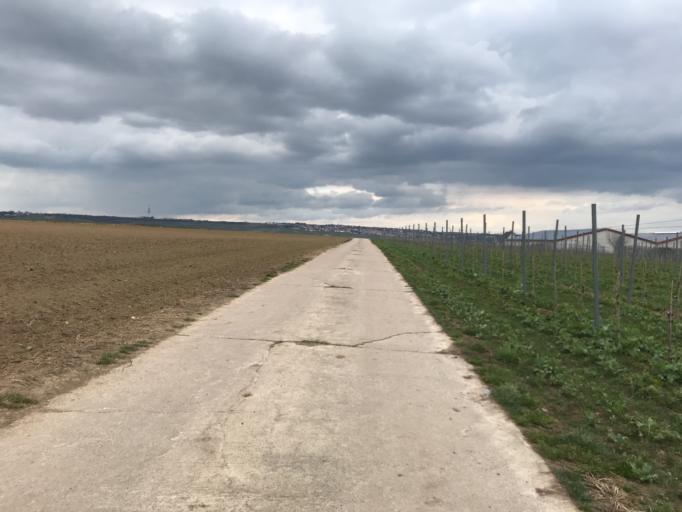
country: DE
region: Rheinland-Pfalz
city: Nieder-Olm
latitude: 49.9037
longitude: 8.1832
